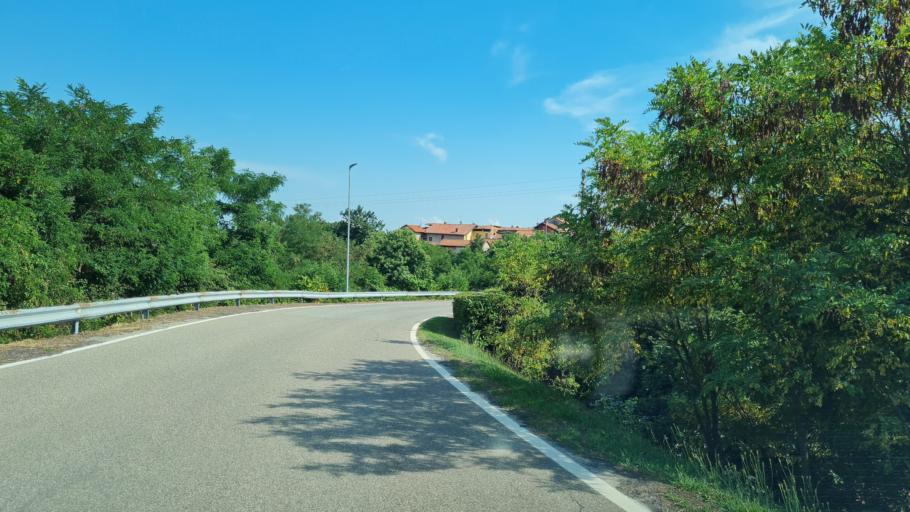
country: IT
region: Piedmont
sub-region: Provincia di Biella
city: Masserano
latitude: 45.5980
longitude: 8.2160
